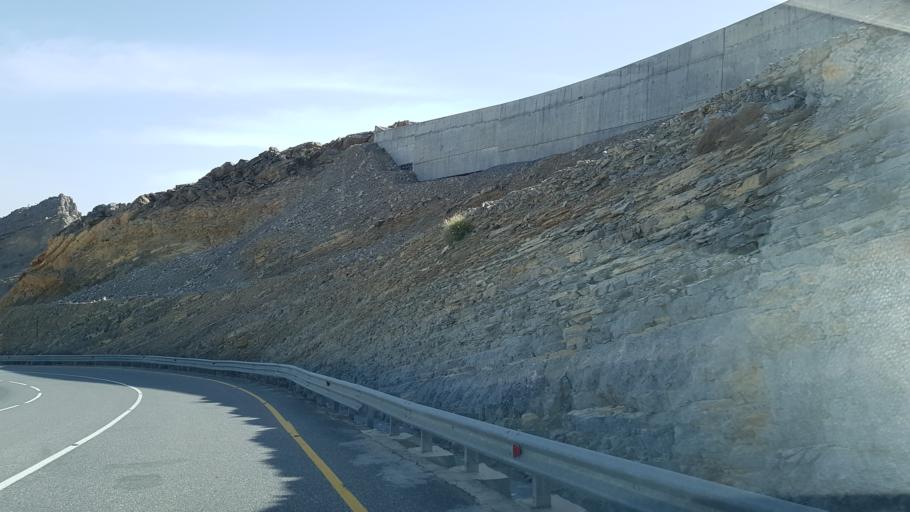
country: OM
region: Muhafazat ad Dakhiliyah
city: Izki
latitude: 23.0194
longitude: 57.6947
